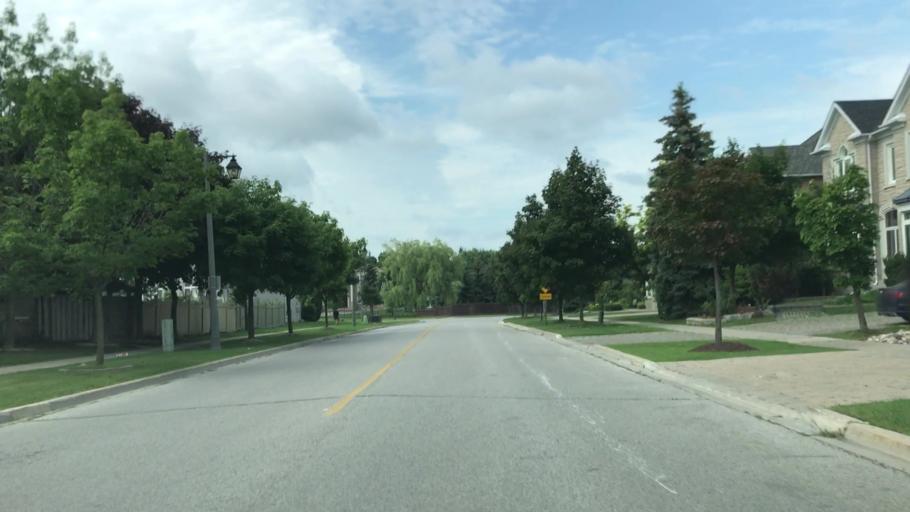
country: CA
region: Ontario
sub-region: York
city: Richmond Hill
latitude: 43.8664
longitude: -79.3928
